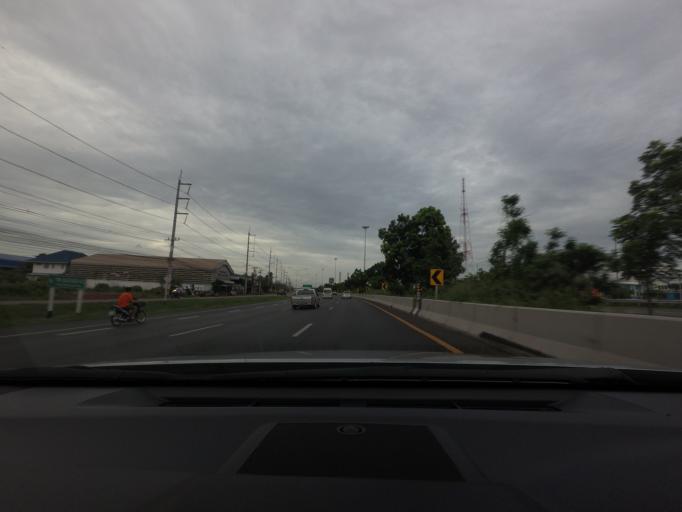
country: TH
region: Samut Songkhram
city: Samut Songkhram
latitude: 13.3850
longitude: 99.9923
